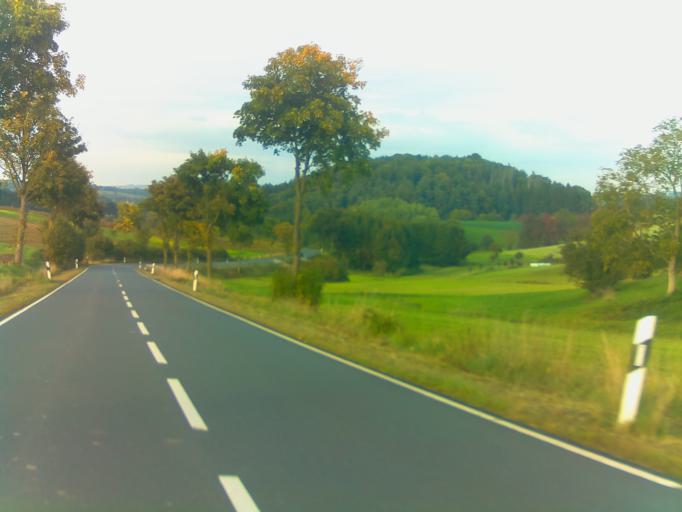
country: DE
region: Hesse
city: Reichelsheim
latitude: 49.7252
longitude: 8.8441
